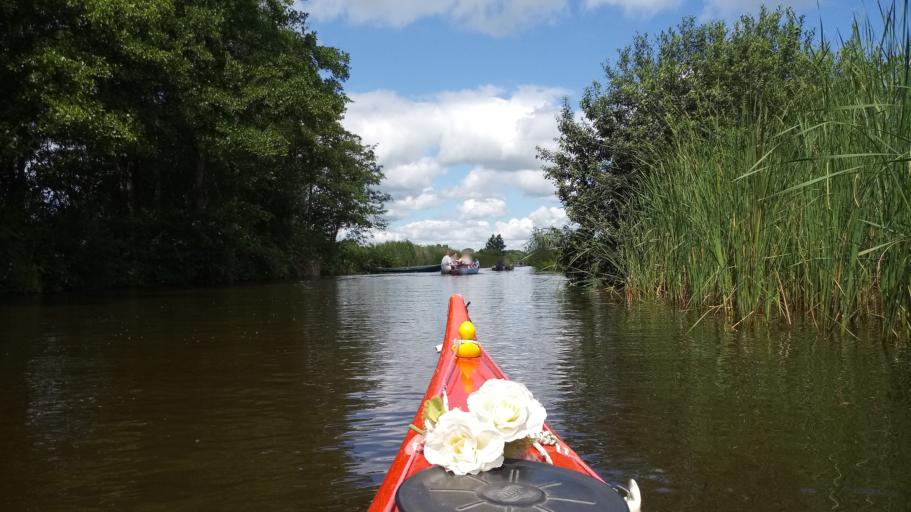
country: NL
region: Overijssel
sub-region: Gemeente Steenwijkerland
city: Wanneperveen
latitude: 52.7139
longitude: 6.1013
